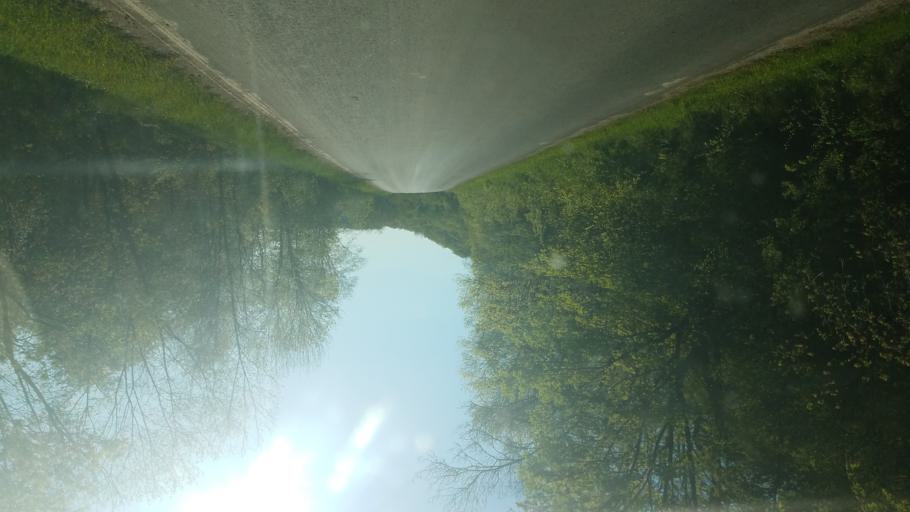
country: US
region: Wisconsin
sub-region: Vernon County
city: Hillsboro
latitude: 43.6259
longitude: -90.4712
